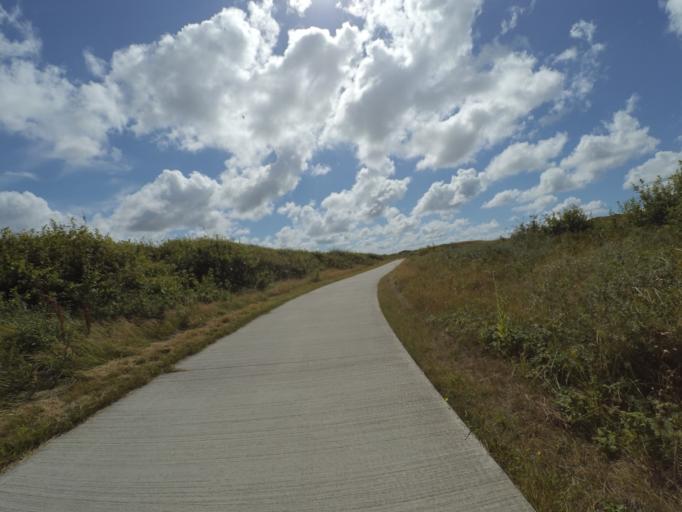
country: NL
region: North Holland
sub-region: Gemeente Texel
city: Den Burg
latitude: 53.1729
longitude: 4.8511
